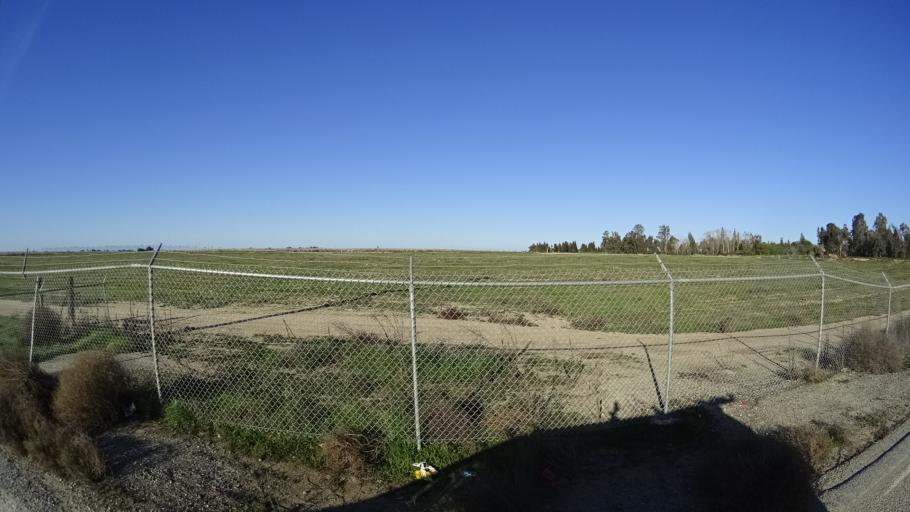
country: US
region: California
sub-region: Fresno County
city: Biola
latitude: 36.7988
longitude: -119.9163
